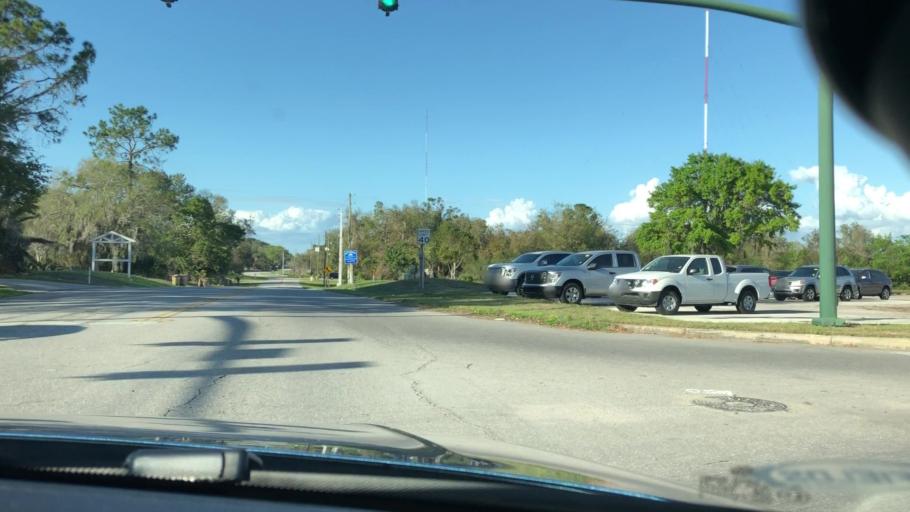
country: US
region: Florida
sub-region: Lake County
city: Silver Lake
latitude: 28.8267
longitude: -81.7871
